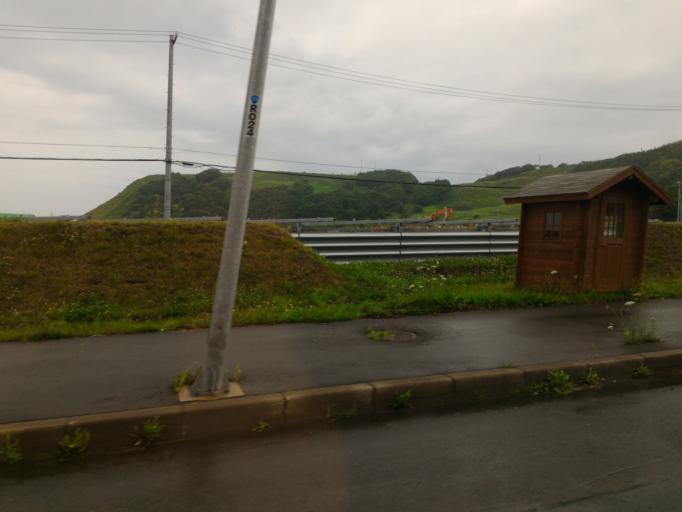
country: JP
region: Hokkaido
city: Rumoi
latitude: 44.0276
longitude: 141.6677
